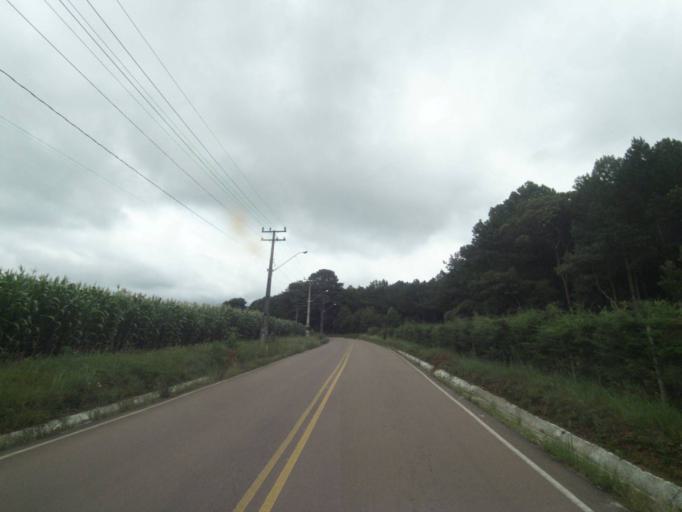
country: BR
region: Parana
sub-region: Campina Grande Do Sul
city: Campina Grande do Sul
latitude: -25.3134
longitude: -49.0309
